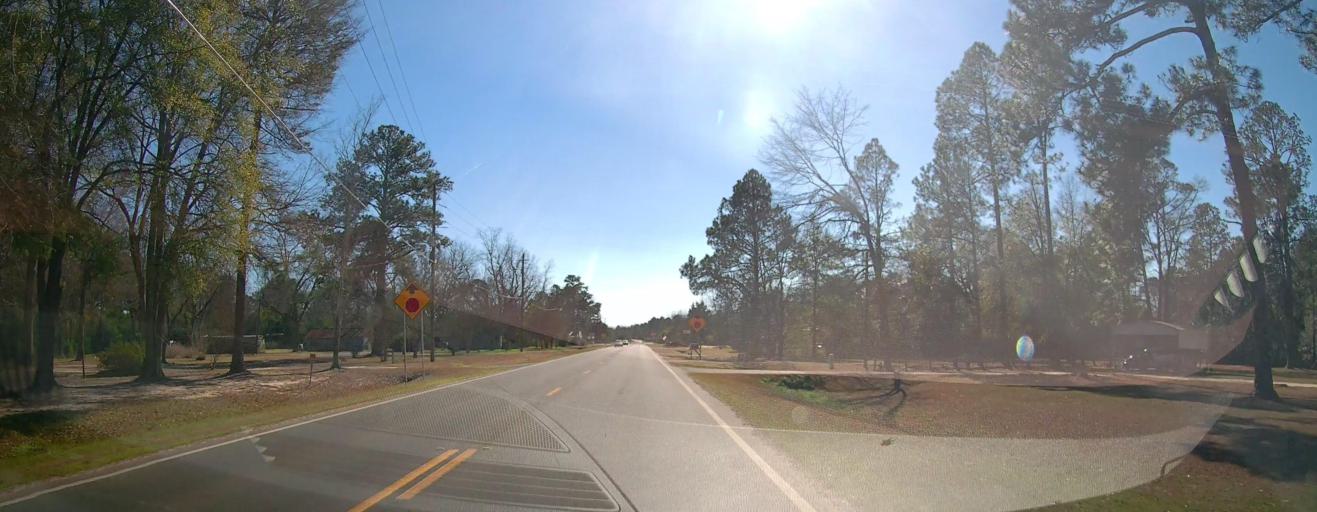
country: US
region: Georgia
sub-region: Macon County
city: Oglethorpe
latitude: 32.2730
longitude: -84.0793
